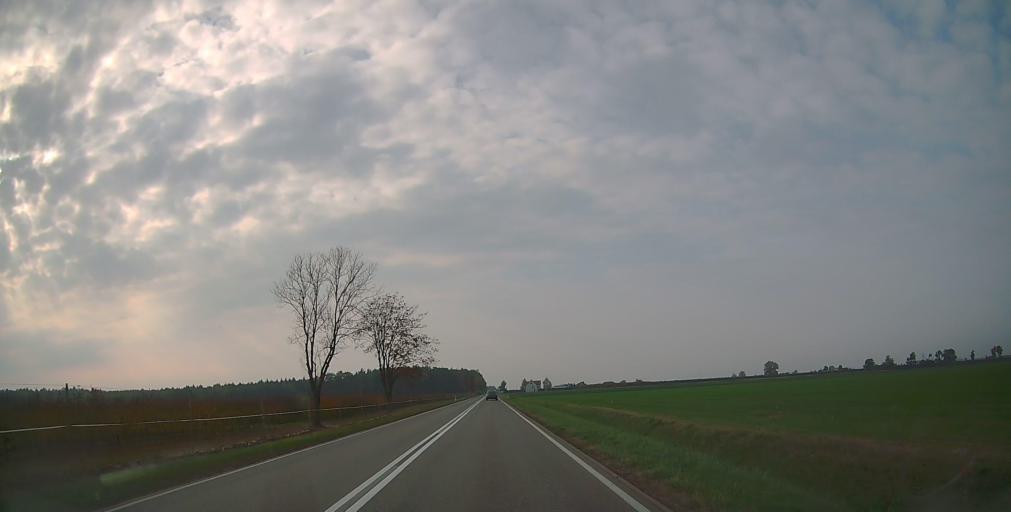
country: PL
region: Masovian Voivodeship
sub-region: Powiat grojecki
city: Belsk Duzy
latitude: 51.8026
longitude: 20.7899
